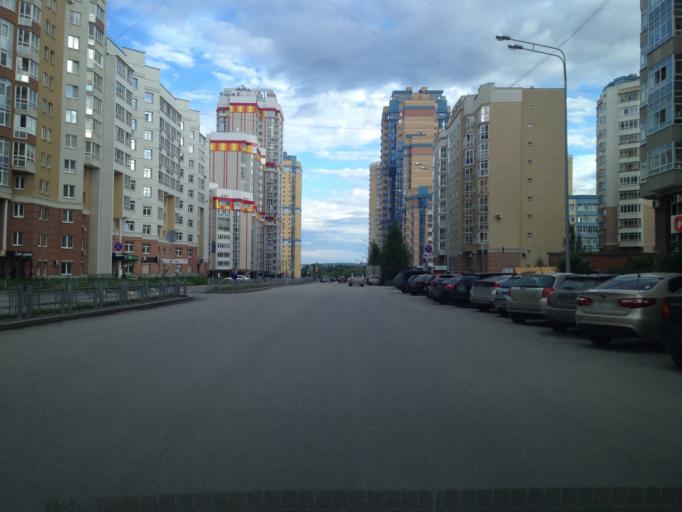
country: RU
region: Sverdlovsk
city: Yekaterinburg
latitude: 56.8067
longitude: 60.6018
